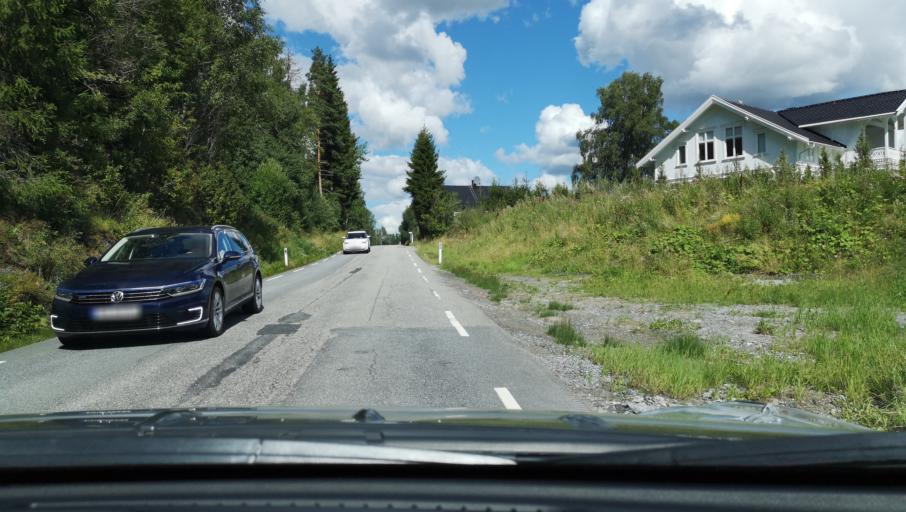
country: NO
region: Ostfold
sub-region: Hobol
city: Elvestad
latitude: 59.6354
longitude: 10.9619
